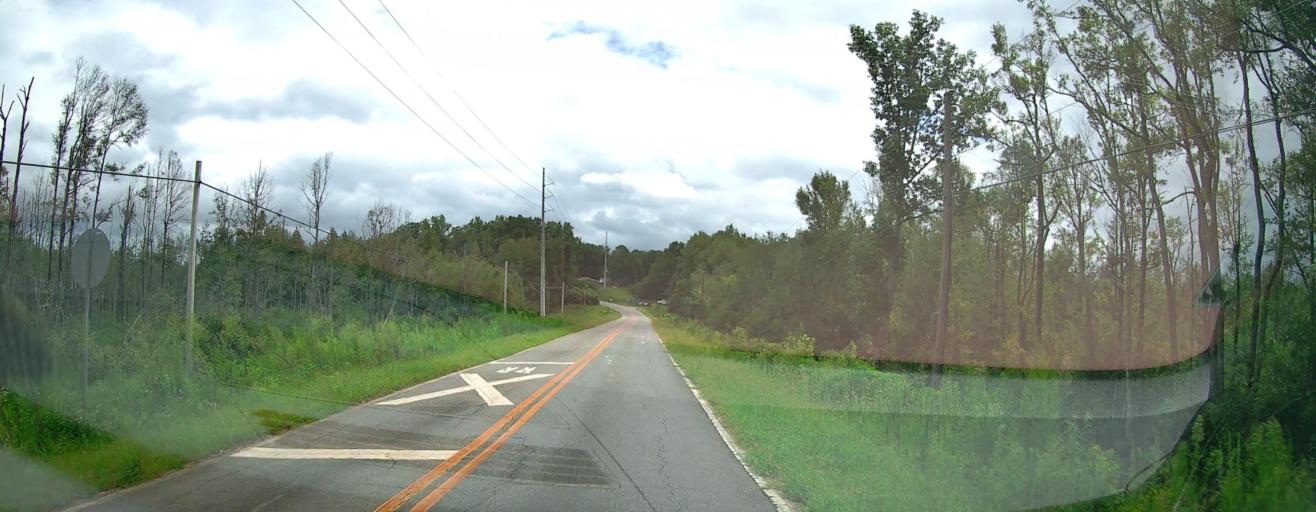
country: US
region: Georgia
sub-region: Bibb County
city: Macon
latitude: 32.8019
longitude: -83.5336
